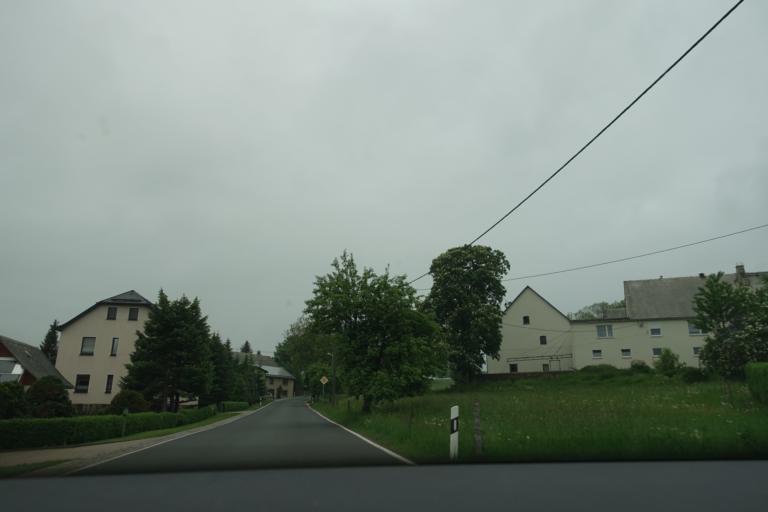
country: DE
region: Saxony
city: Eppendorf
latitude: 50.7866
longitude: 13.2709
